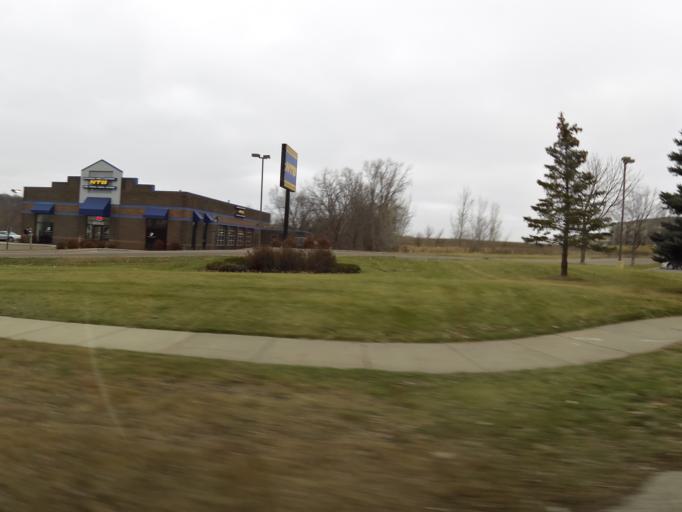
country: US
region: Minnesota
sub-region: Scott County
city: Prior Lake
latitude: 44.7465
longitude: -93.3857
